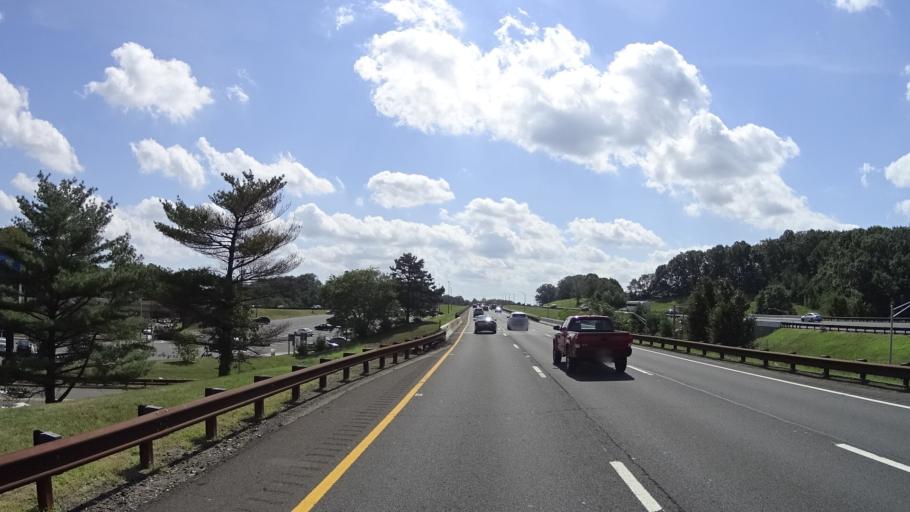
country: US
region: New Jersey
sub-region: Middlesex County
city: South Amboy
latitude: 40.4640
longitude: -74.2867
